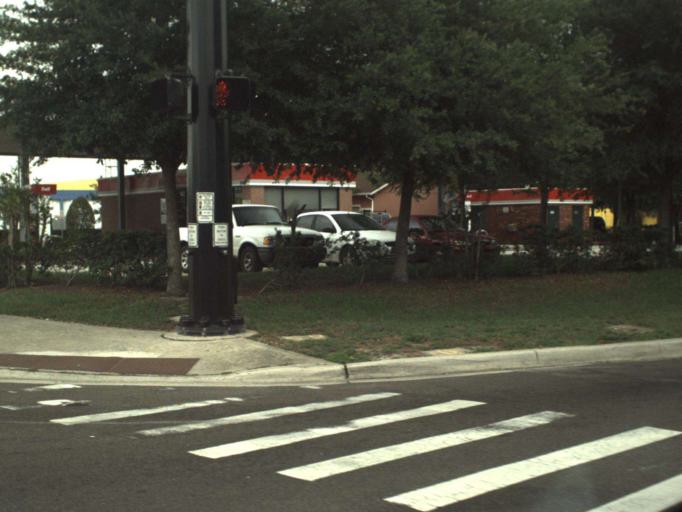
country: US
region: Florida
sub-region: Seminole County
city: Altamonte Springs
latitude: 28.6631
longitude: -81.3579
